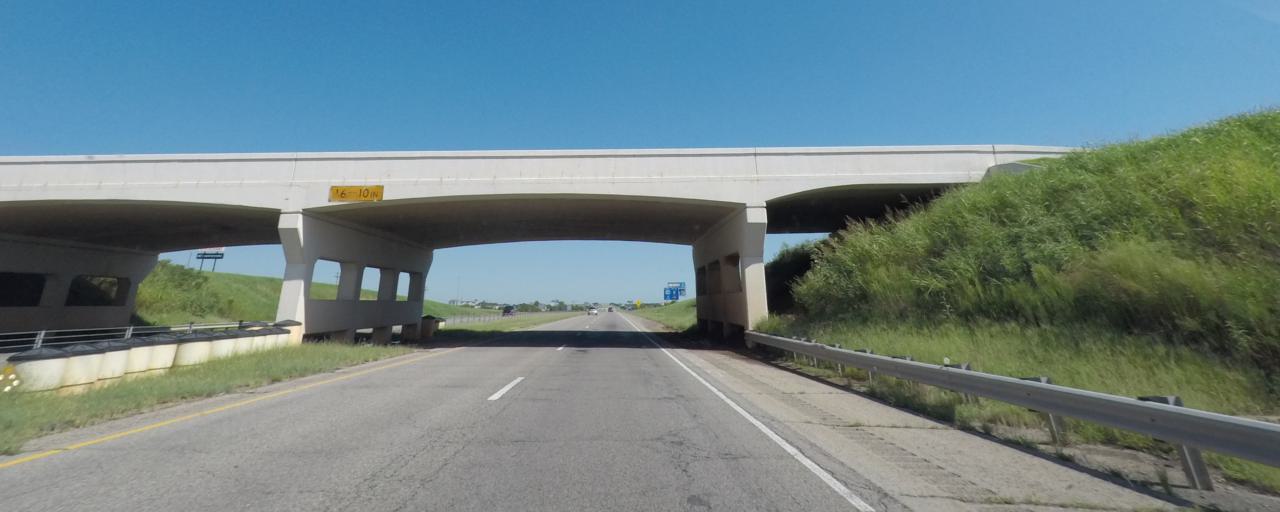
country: US
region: Oklahoma
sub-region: Noble County
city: Perry
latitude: 36.2748
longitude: -97.3276
